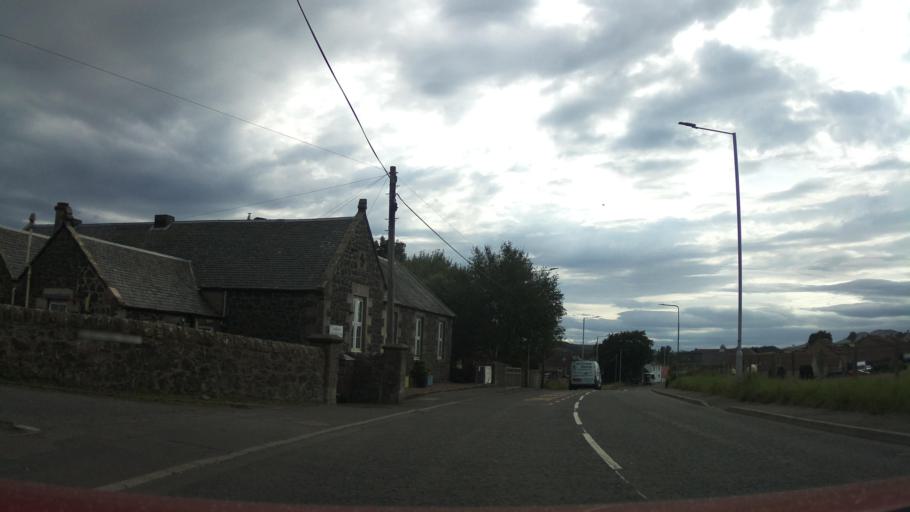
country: GB
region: Scotland
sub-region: Fife
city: Strathkinness
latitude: 56.2581
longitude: -2.8578
